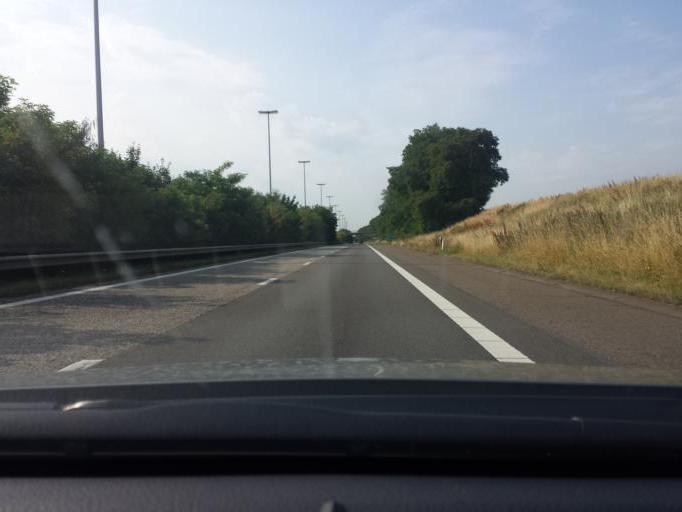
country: BE
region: Flanders
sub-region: Provincie Limburg
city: Hoeselt
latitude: 50.8133
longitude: 5.5158
